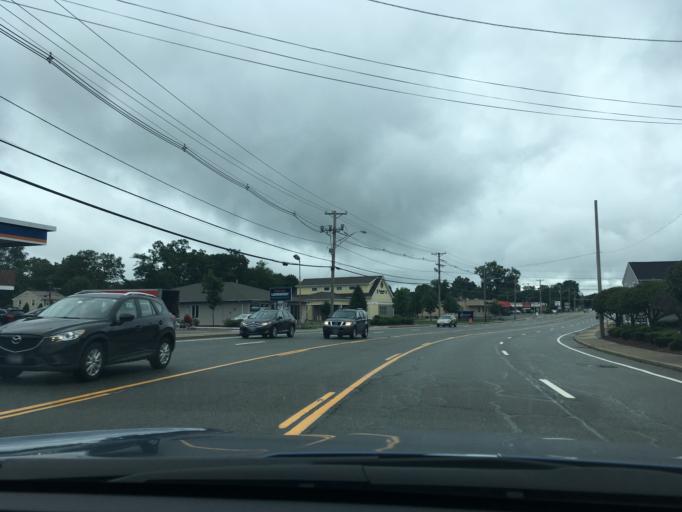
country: US
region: Rhode Island
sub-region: Kent County
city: East Greenwich
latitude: 41.6405
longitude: -71.4685
